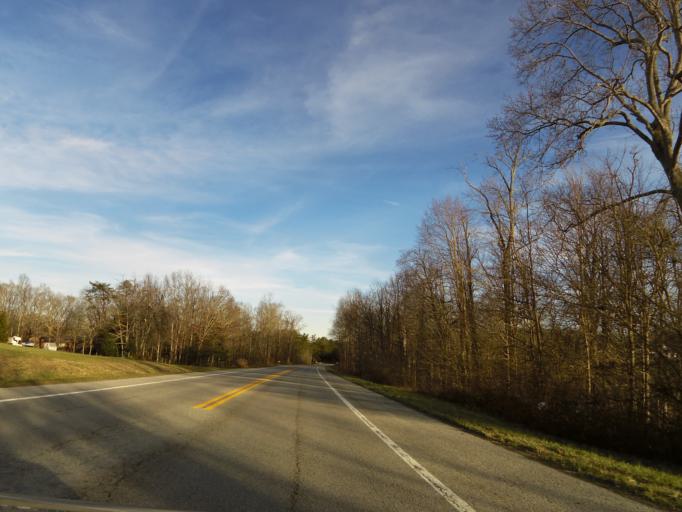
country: US
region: Tennessee
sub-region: Cumberland County
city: Crossville
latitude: 35.9542
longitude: -85.1104
